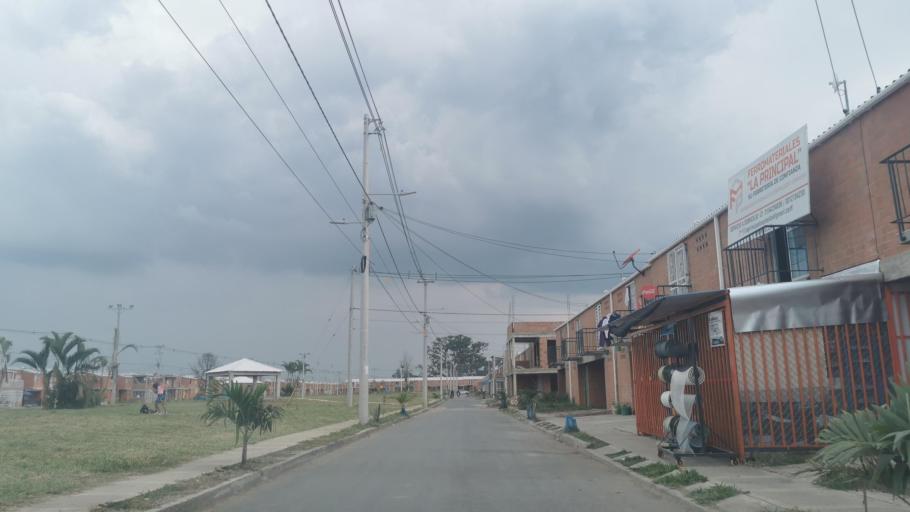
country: CO
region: Valle del Cauca
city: Jamundi
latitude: 3.2360
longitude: -76.5265
